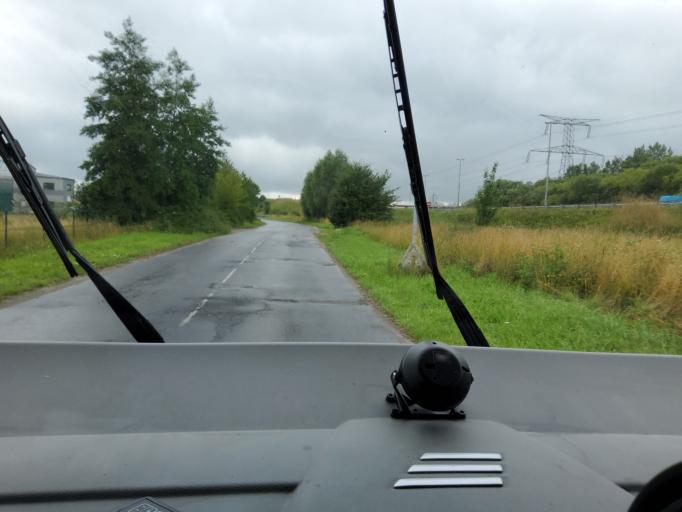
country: FR
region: Nord-Pas-de-Calais
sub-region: Departement du Pas-de-Calais
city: Saint-Folquin
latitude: 50.9516
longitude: 2.1312
